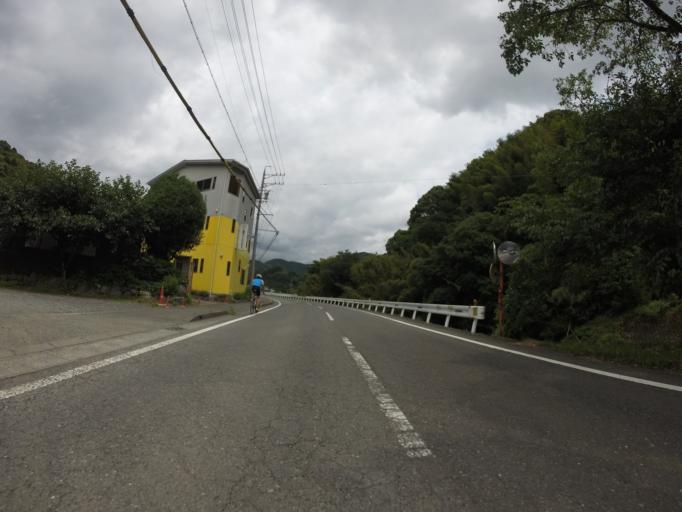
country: JP
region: Shizuoka
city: Shizuoka-shi
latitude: 34.9966
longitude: 138.3098
